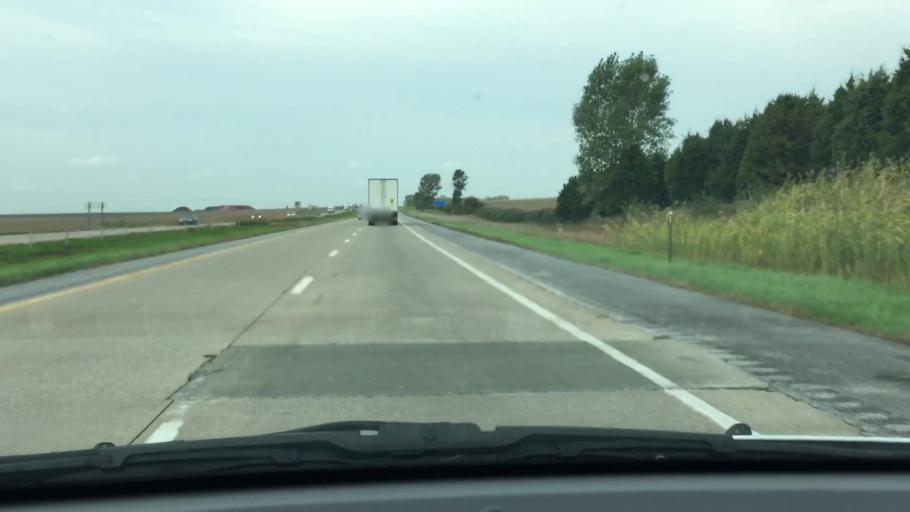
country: US
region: Iowa
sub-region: Cedar County
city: Durant
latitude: 41.6332
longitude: -90.9033
